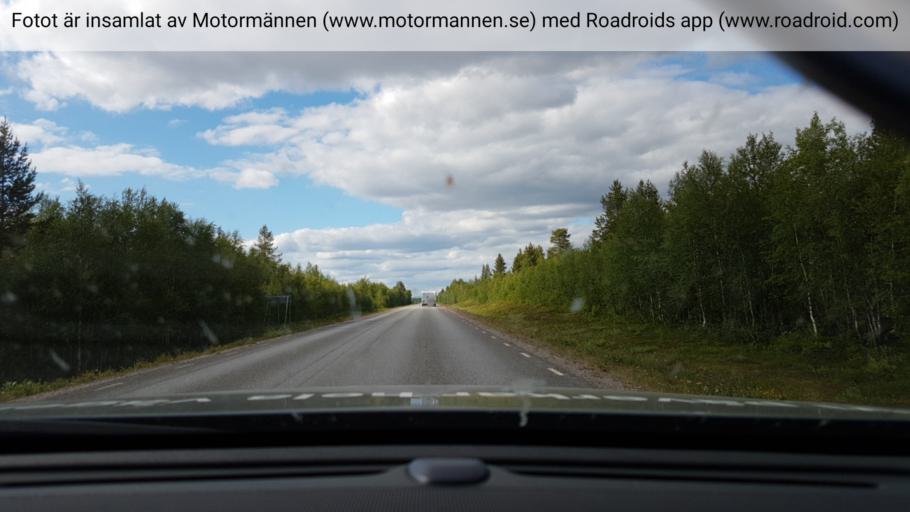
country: SE
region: Norrbotten
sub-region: Arjeplogs Kommun
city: Arjeplog
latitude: 66.1552
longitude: 17.3435
